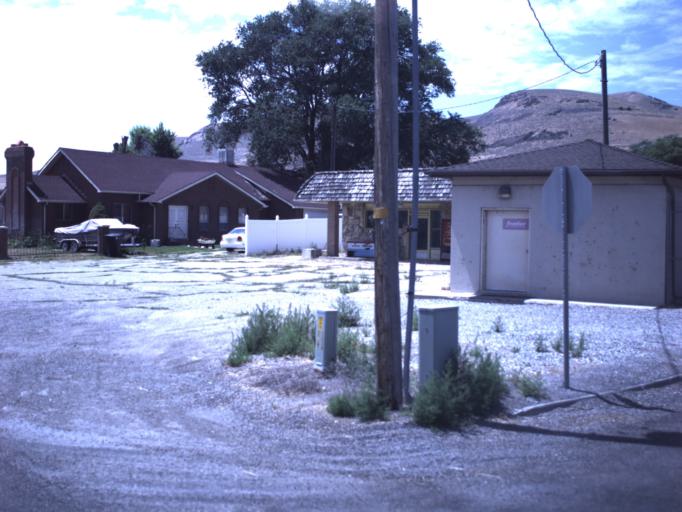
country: US
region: Utah
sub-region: Box Elder County
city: Tremonton
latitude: 41.6928
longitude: -112.2952
